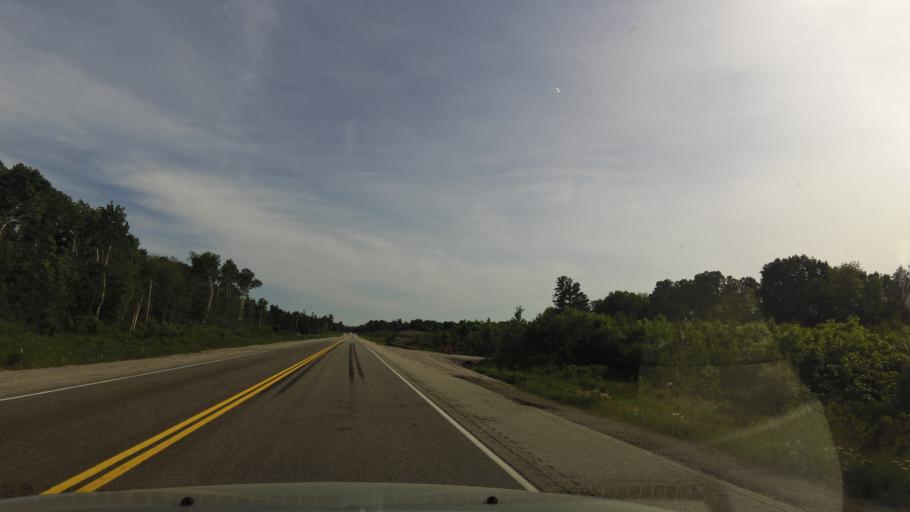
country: CA
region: Ontario
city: Greater Sudbury
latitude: 45.9423
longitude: -80.5823
